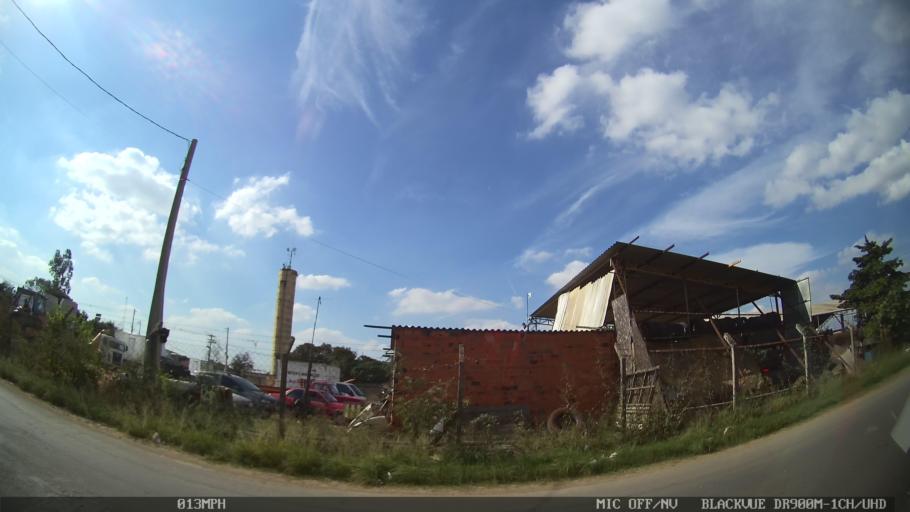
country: BR
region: Sao Paulo
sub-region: Hortolandia
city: Hortolandia
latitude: -22.9059
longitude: -47.2480
